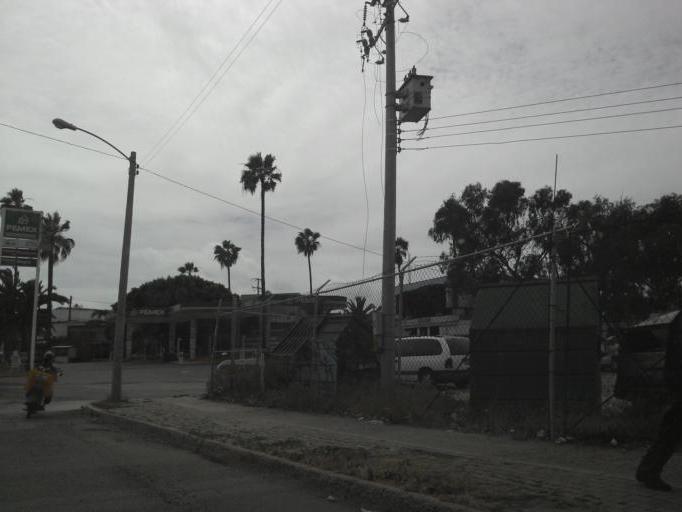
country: US
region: California
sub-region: San Diego County
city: Imperial Beach
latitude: 32.5301
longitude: -117.1182
